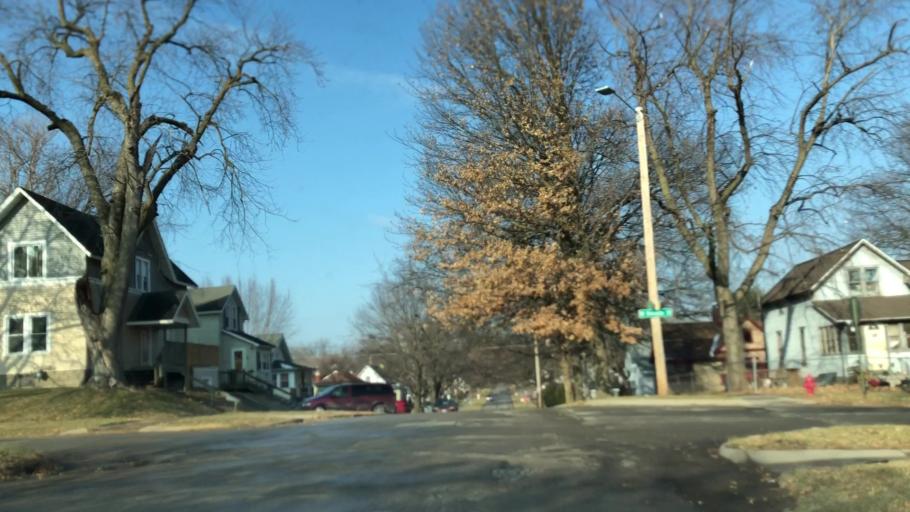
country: US
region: Iowa
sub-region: Marshall County
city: Marshalltown
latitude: 42.0441
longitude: -92.9193
